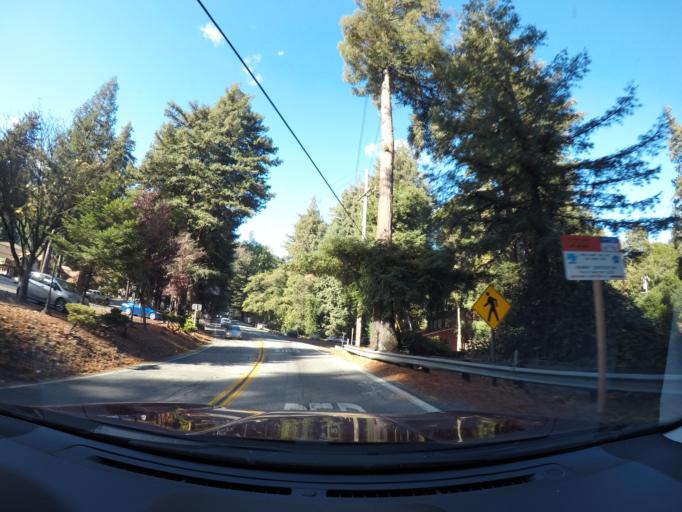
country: US
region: California
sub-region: Santa Cruz County
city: Brookdale
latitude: 37.1077
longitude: -122.1081
